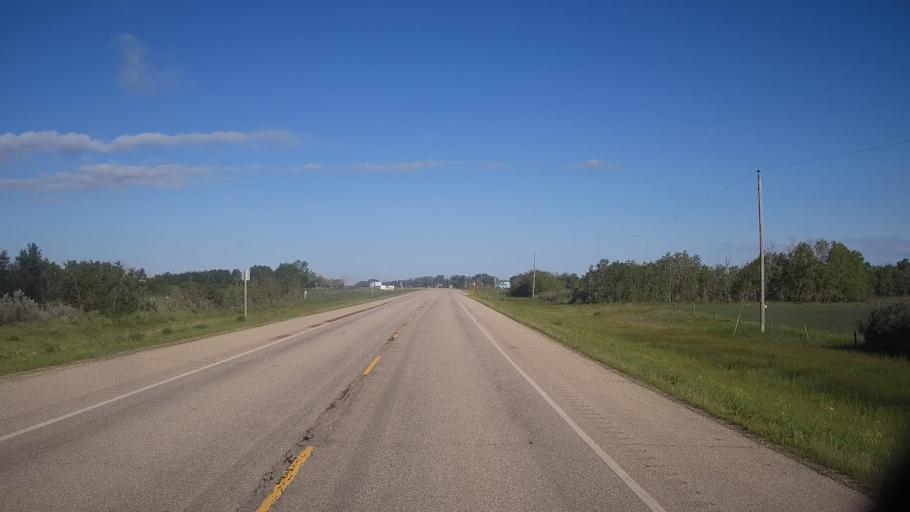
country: CA
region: Saskatchewan
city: Lanigan
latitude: 51.8723
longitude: -105.1768
